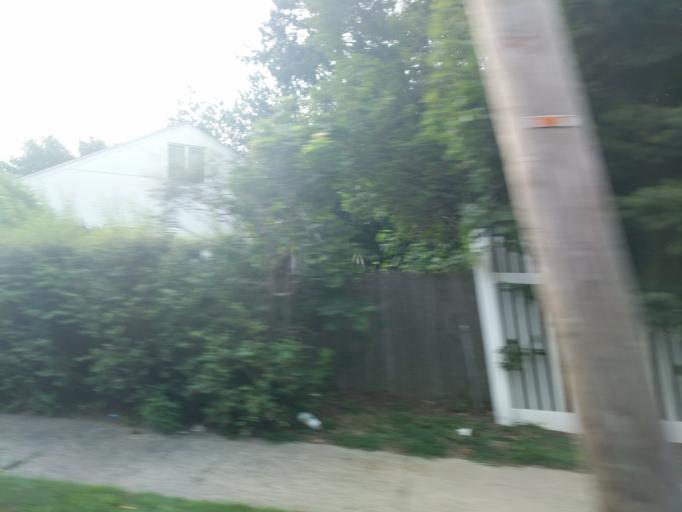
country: US
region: New York
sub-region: Nassau County
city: East Rockaway
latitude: 40.6409
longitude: -73.6756
